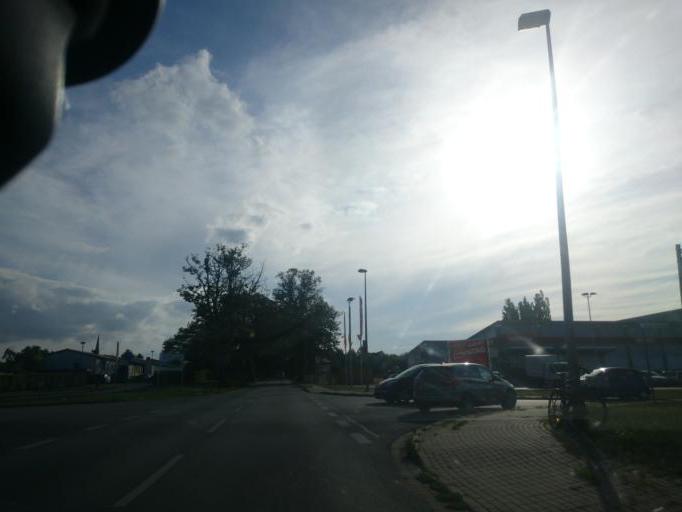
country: DE
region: Mecklenburg-Vorpommern
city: Bad Doberan
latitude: 54.1144
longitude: 11.9120
